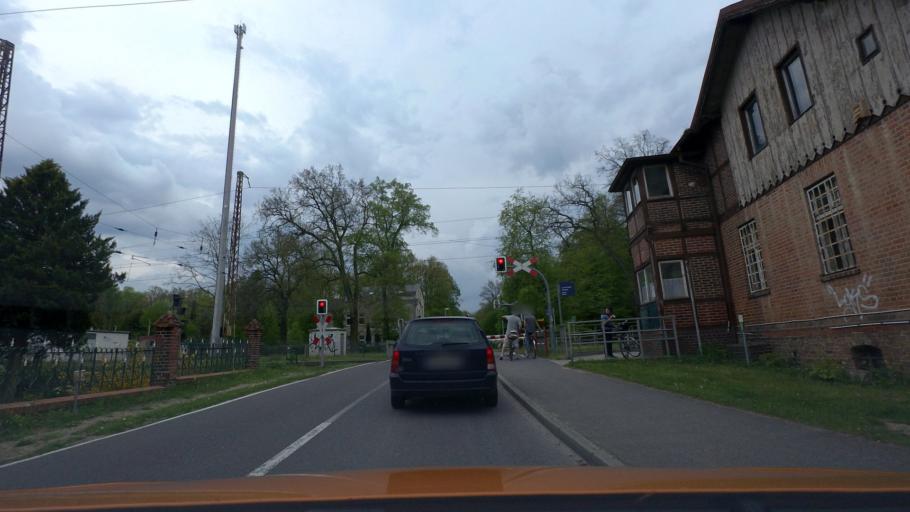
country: DE
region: Brandenburg
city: Spreenhagen
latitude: 52.4004
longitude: 13.9217
